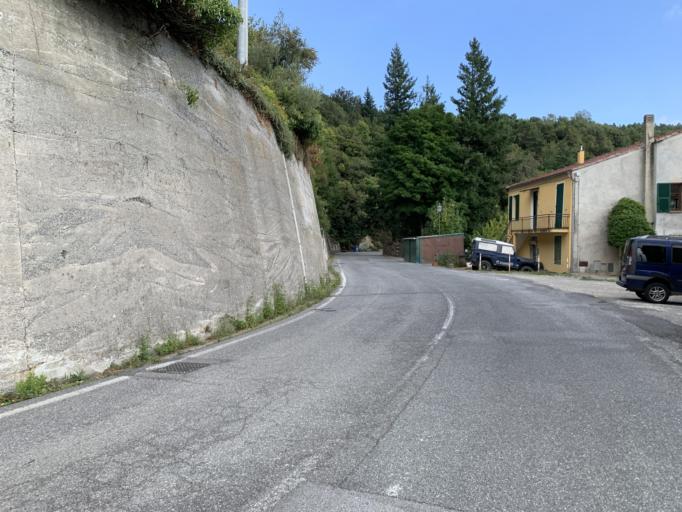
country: IT
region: Liguria
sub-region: Provincia di Savona
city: Orco Feglino
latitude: 44.2215
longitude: 8.3058
